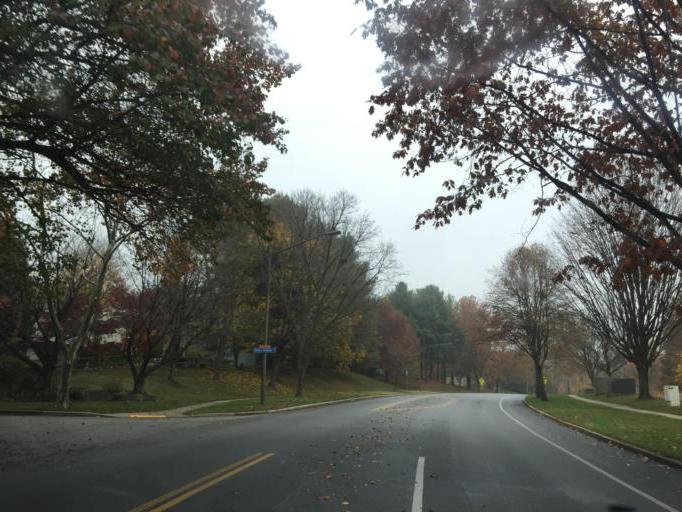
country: US
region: Maryland
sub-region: Howard County
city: Riverside
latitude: 39.1885
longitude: -76.8399
